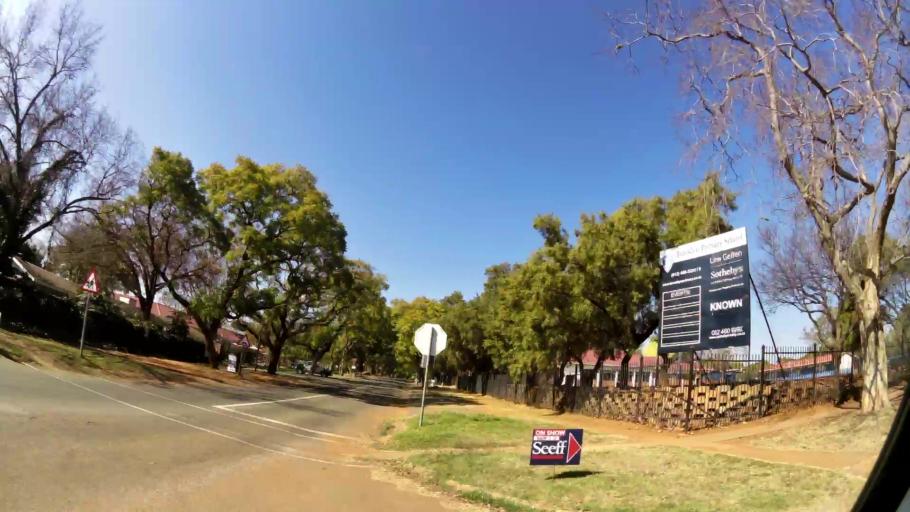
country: ZA
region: Gauteng
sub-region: City of Tshwane Metropolitan Municipality
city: Pretoria
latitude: -25.7640
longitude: 28.2421
